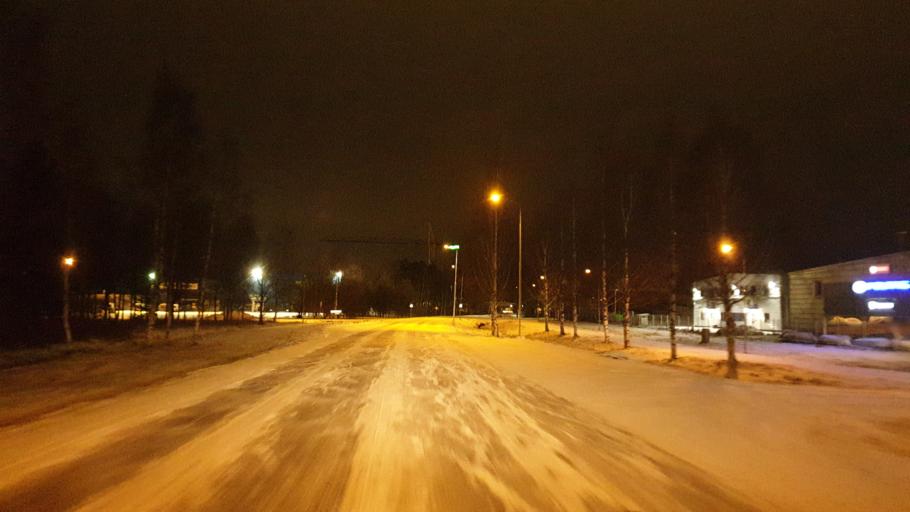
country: FI
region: Northern Ostrobothnia
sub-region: Oulu
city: Oulu
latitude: 64.9948
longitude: 25.4510
